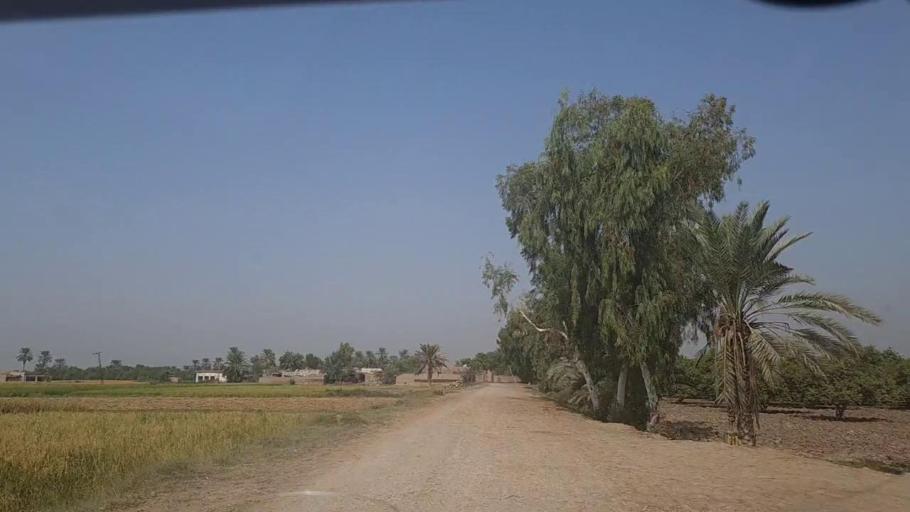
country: PK
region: Sindh
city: Madeji
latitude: 27.8053
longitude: 68.4263
